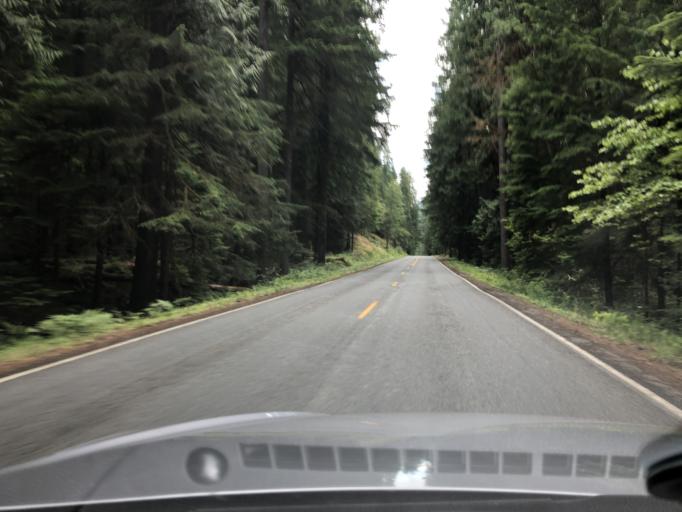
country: US
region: Washington
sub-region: Pierce County
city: Buckley
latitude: 46.7252
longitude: -121.5742
